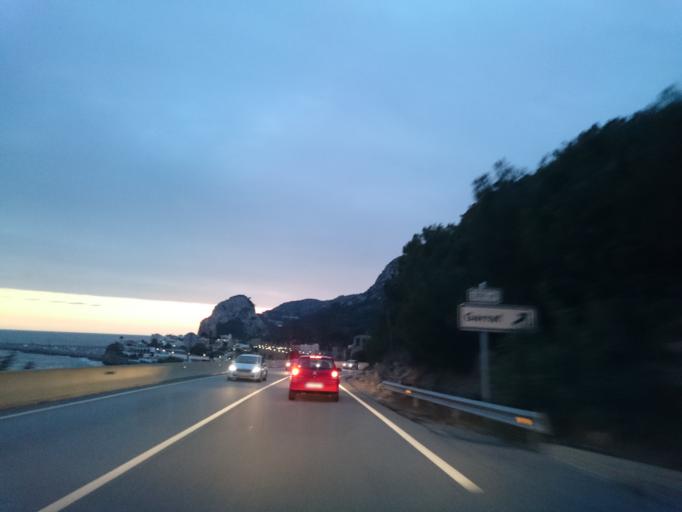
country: ES
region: Catalonia
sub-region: Provincia de Barcelona
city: Castelldefels
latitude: 41.2559
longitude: 1.9075
